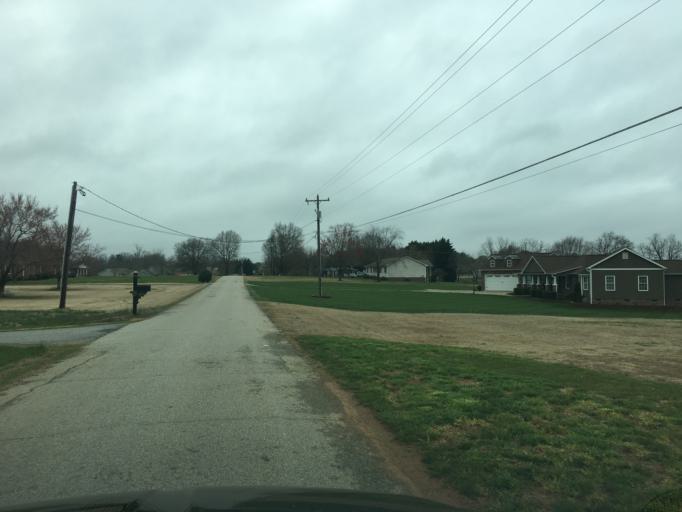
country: US
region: South Carolina
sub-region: Spartanburg County
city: Inman Mills
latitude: 35.0259
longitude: -82.1148
